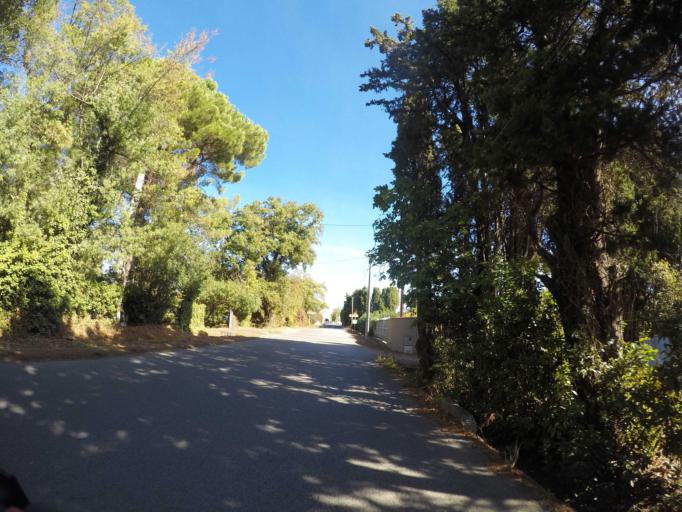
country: FR
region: Languedoc-Roussillon
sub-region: Departement des Pyrenees-Orientales
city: Le Soler
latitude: 42.6774
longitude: 2.7910
